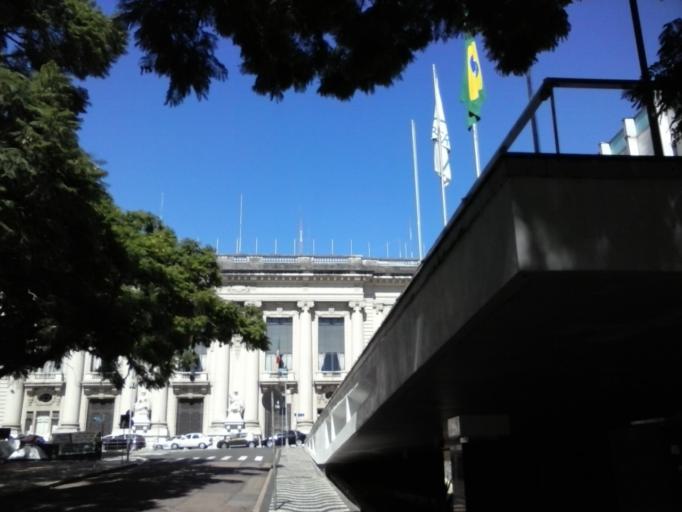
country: BR
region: Rio Grande do Sul
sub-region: Porto Alegre
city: Porto Alegre
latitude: -30.0327
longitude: -51.2305
